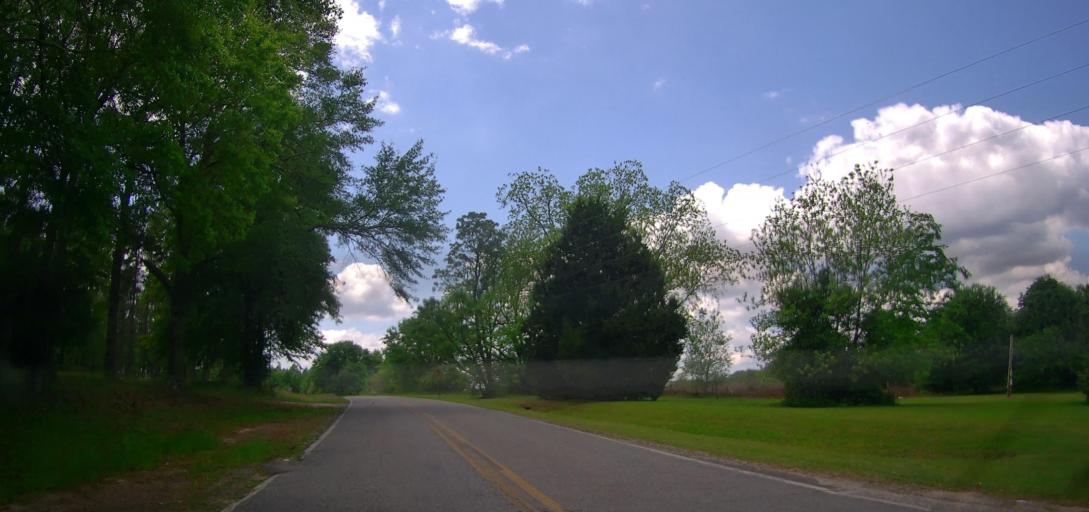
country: US
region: Georgia
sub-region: Laurens County
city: Dublin
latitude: 32.6017
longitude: -82.9244
